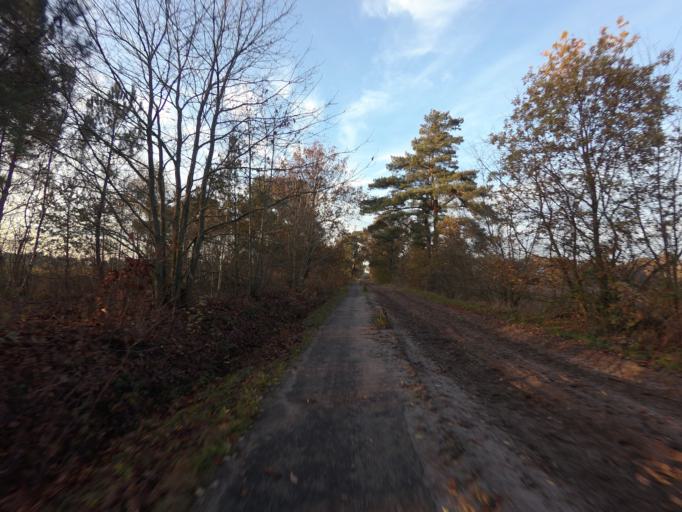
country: NL
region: North Brabant
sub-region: Gemeente Breda
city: Breda
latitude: 51.5076
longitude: 4.8219
